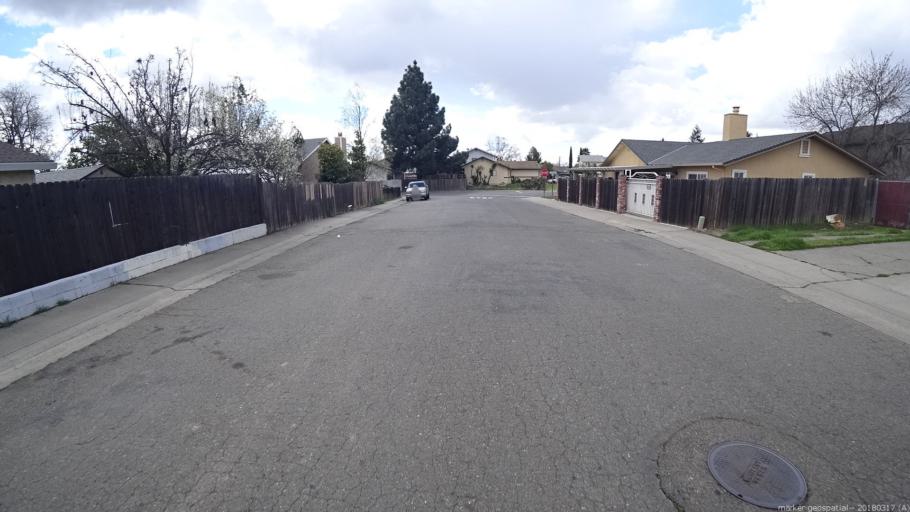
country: US
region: California
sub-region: Sacramento County
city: Florin
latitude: 38.4763
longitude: -121.4052
